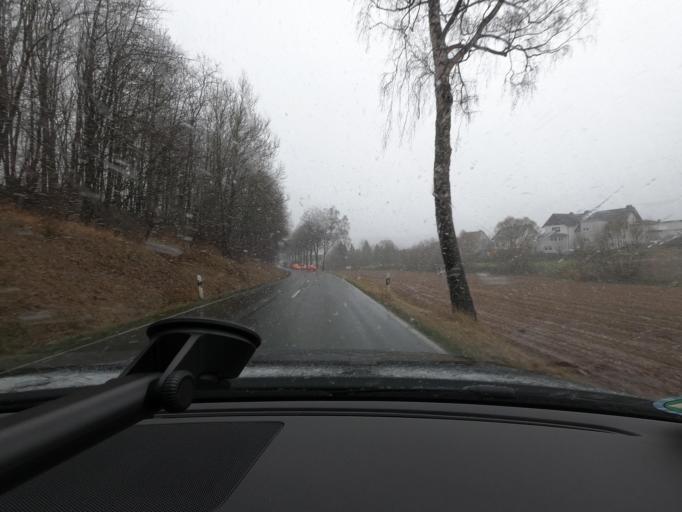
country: DE
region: North Rhine-Westphalia
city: Marsberg
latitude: 51.4980
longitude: 8.9104
